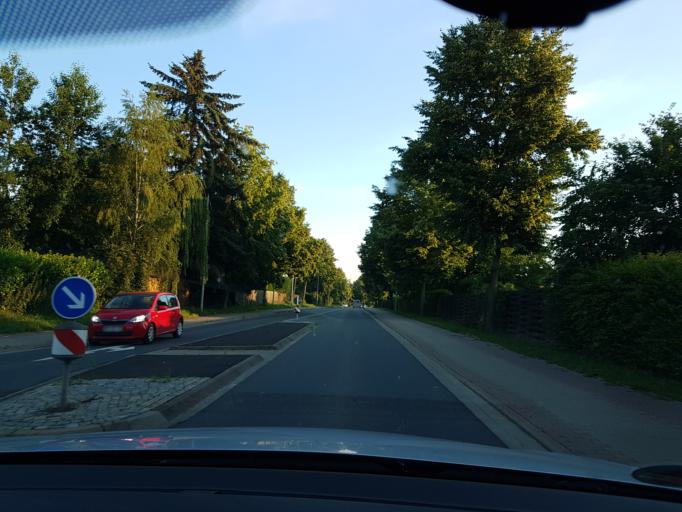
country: DE
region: Lower Saxony
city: Schoningen
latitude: 52.1550
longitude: 10.9655
